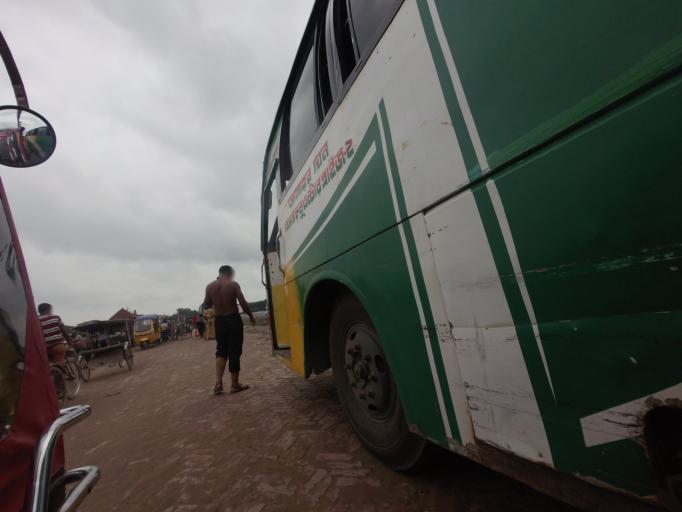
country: BD
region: Khulna
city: Kalia
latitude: 23.1944
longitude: 89.6888
